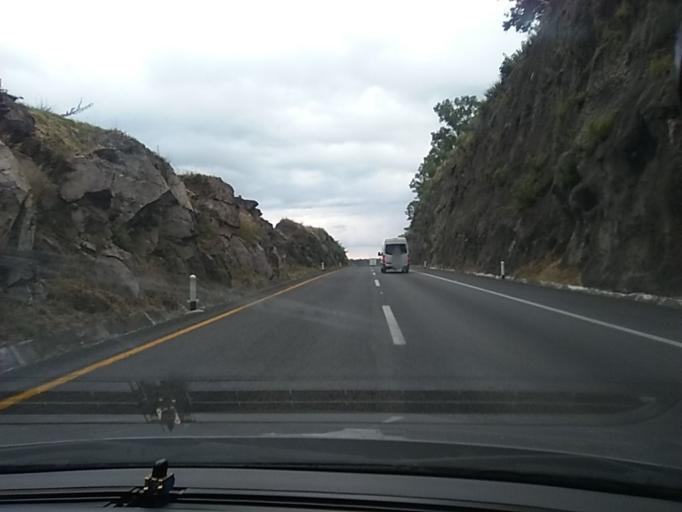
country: MX
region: Jalisco
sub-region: Zapotlan del Rey
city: Zapotlan del Rey
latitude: 20.5148
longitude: -102.9747
